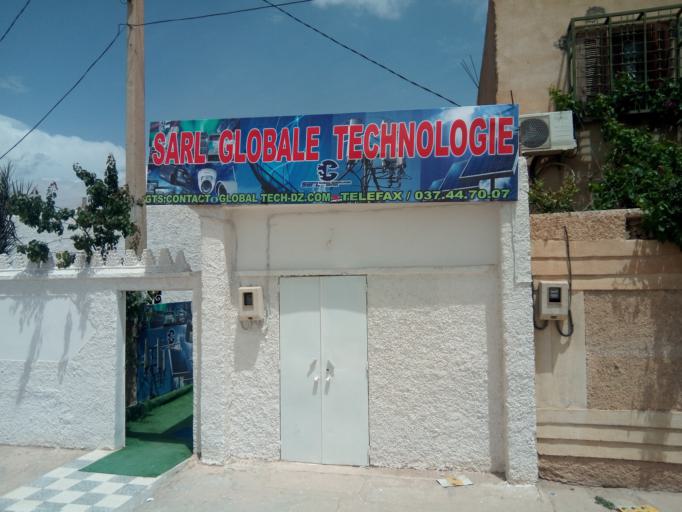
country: DZ
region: Tebessa
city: Bir el Ater
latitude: 34.7550
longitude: 8.0538
